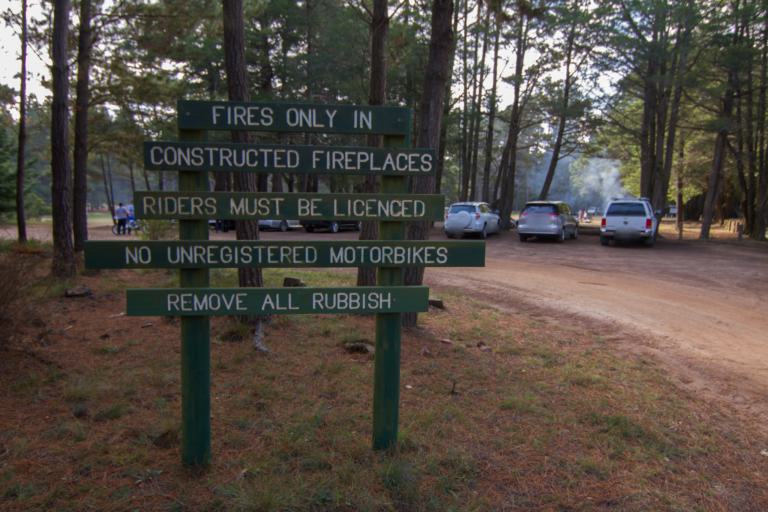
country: AU
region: New South Wales
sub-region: Wingecarribee
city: Moss Vale
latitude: -34.5282
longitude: 150.2419
